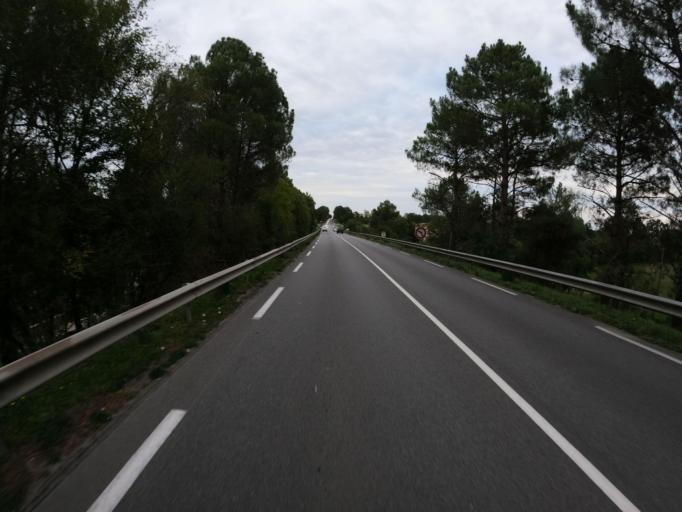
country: FR
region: Poitou-Charentes
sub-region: Departement des Deux-Sevres
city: La Peyratte
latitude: 46.6490
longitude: -0.1882
